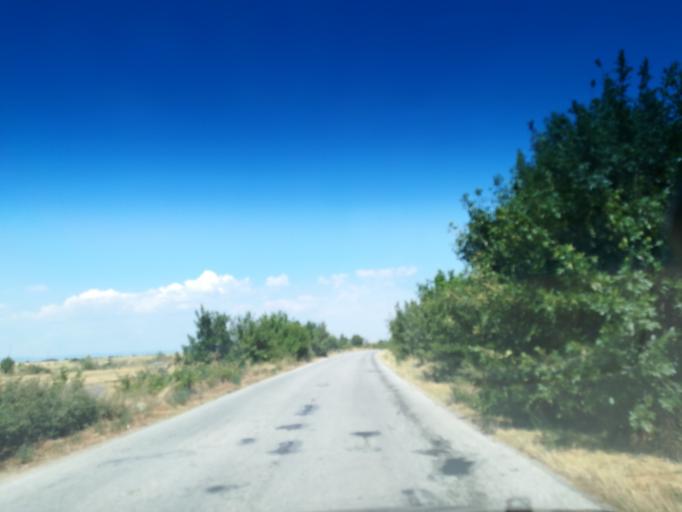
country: BG
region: Stara Zagora
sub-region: Obshtina Chirpan
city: Chirpan
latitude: 42.0585
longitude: 25.1574
